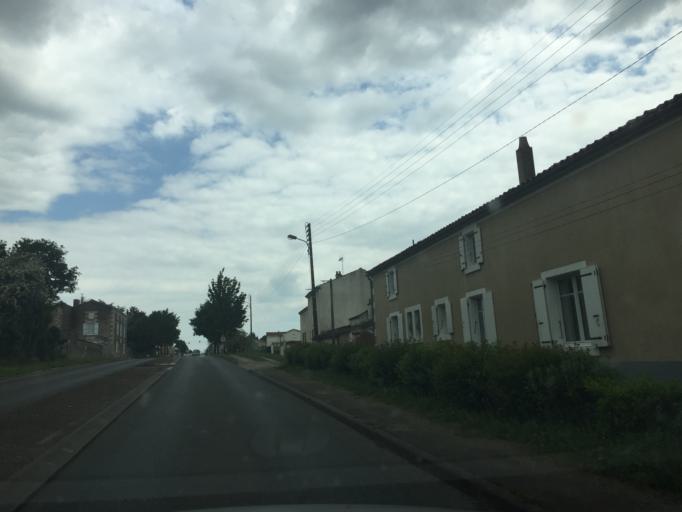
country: FR
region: Pays de la Loire
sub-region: Departement de la Vendee
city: Benet
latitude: 46.3745
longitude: -0.5881
